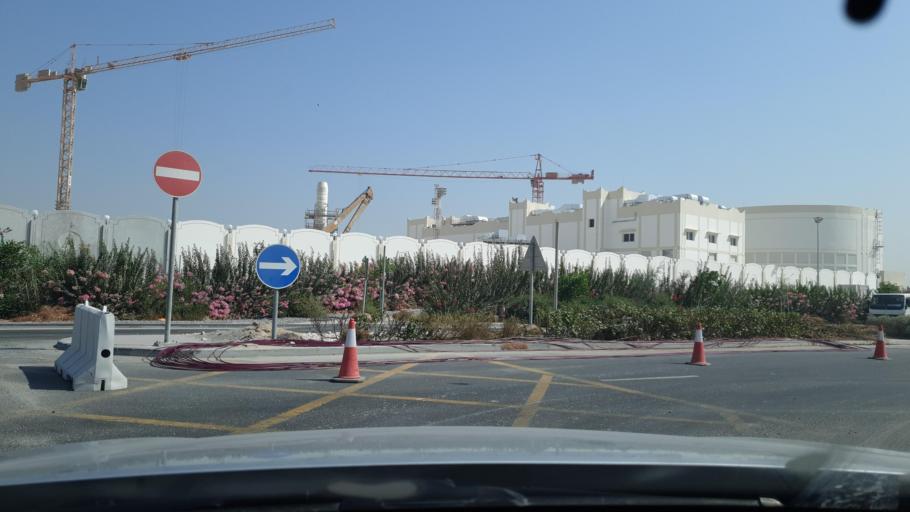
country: QA
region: Baladiyat ad Dawhah
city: Doha
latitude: 25.2324
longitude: 51.5231
